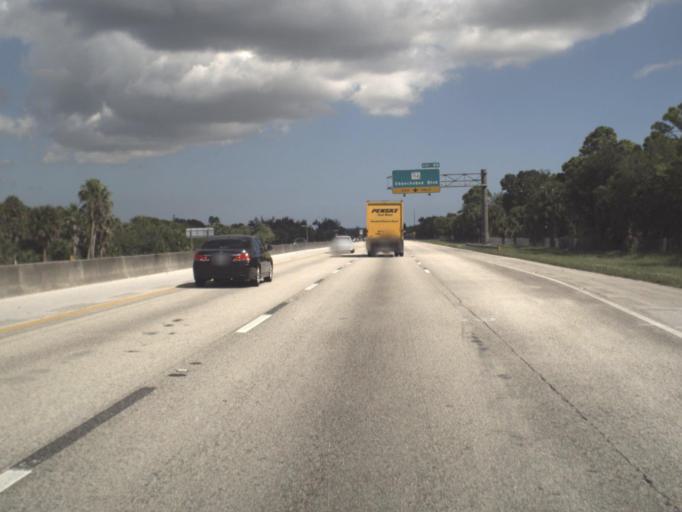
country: US
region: Florida
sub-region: Palm Beach County
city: Plantation Mobile Home Park
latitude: 26.7018
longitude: -80.1466
